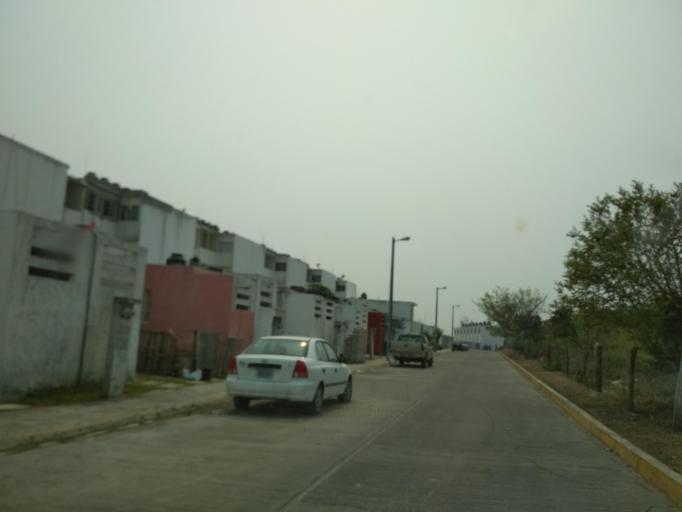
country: MX
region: Veracruz
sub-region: Veracruz
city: Las Amapolas
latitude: 19.1400
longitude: -96.2189
